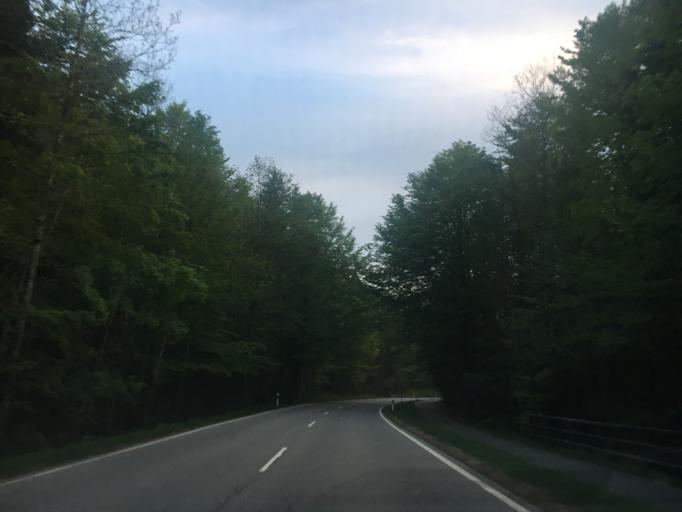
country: DE
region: Bavaria
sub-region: Upper Bavaria
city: Lenggries
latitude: 47.6028
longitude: 11.5766
